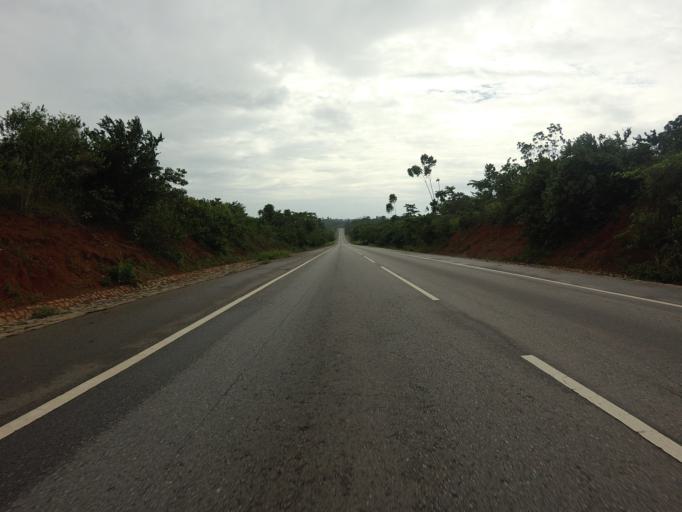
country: GH
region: Eastern
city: Nkawkaw
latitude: 6.5599
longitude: -0.8030
